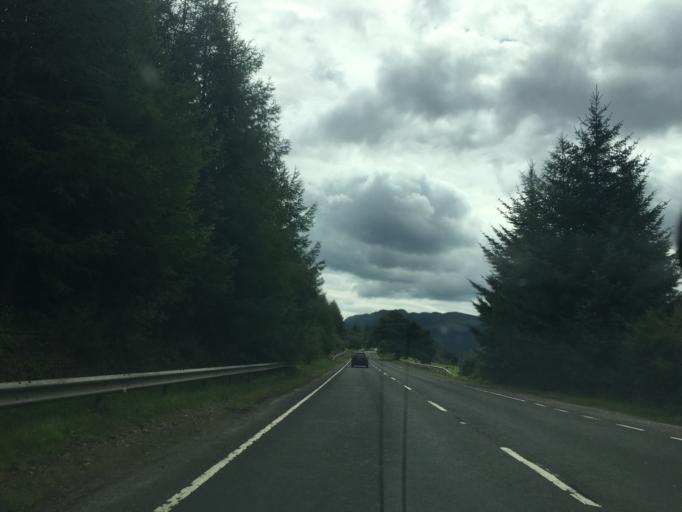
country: GB
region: Scotland
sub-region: Stirling
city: Callander
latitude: 56.3465
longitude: -4.3276
